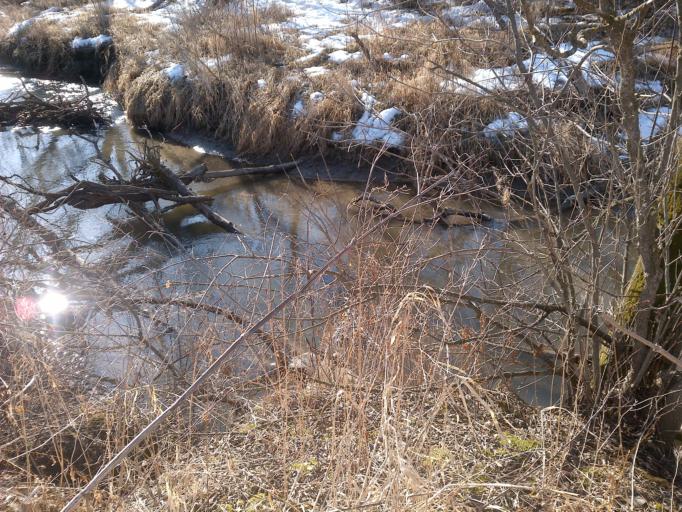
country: US
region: Minnesota
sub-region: Wabasha County
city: Lake City
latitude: 44.4384
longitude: -92.3423
